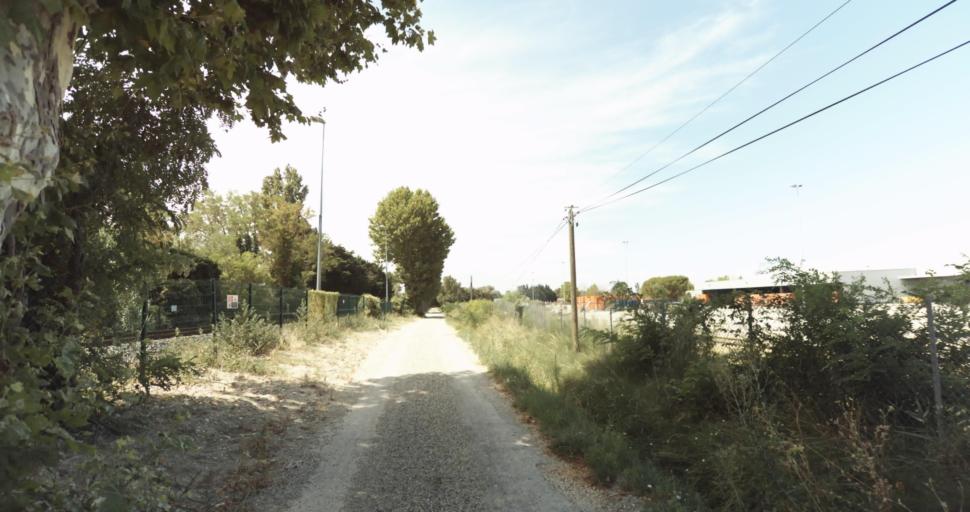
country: FR
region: Provence-Alpes-Cote d'Azur
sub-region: Departement du Vaucluse
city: Monteux
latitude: 44.0320
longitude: 4.9732
